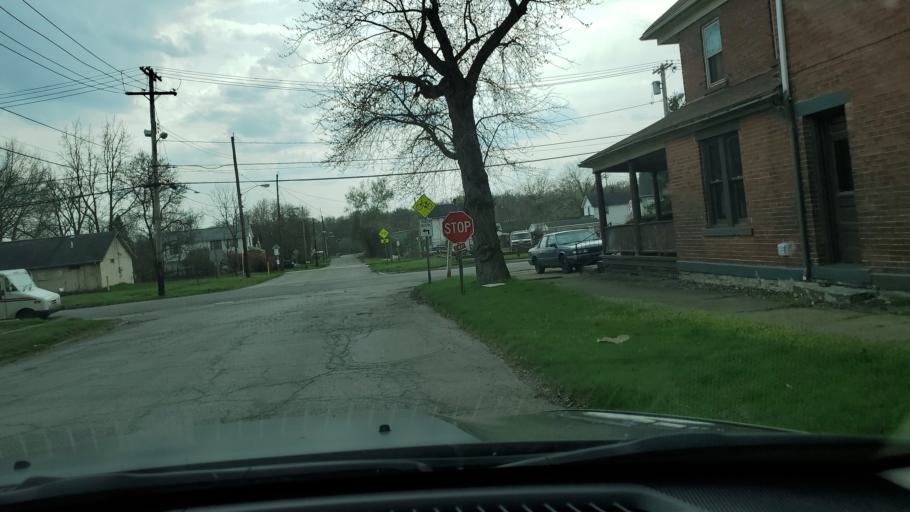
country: US
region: Ohio
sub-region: Trumbull County
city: Niles
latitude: 41.1791
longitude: -80.7585
